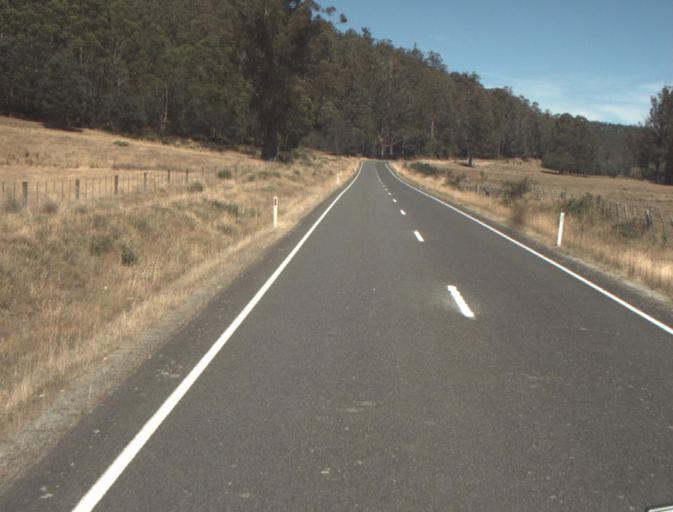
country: AU
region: Tasmania
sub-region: Dorset
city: Scottsdale
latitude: -41.2940
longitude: 147.3853
